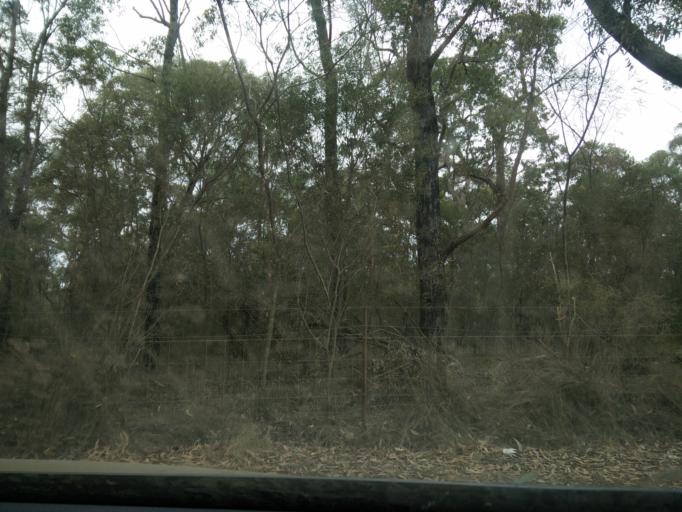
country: AU
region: New South Wales
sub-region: Penrith Municipality
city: Mulgoa
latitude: -33.8404
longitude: 150.5812
